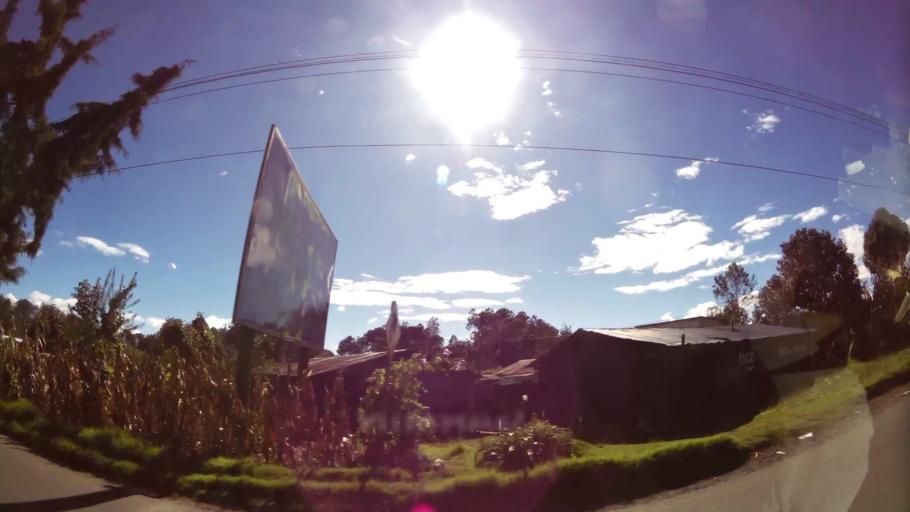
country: GT
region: Solola
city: Solola
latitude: 14.8122
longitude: -91.1802
